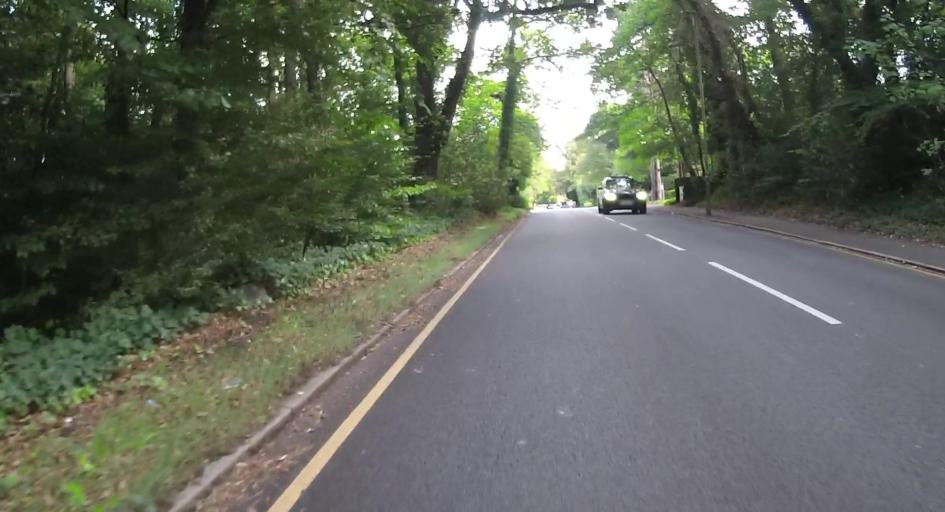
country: GB
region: England
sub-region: Surrey
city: Weybridge
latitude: 51.3636
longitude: -0.4526
